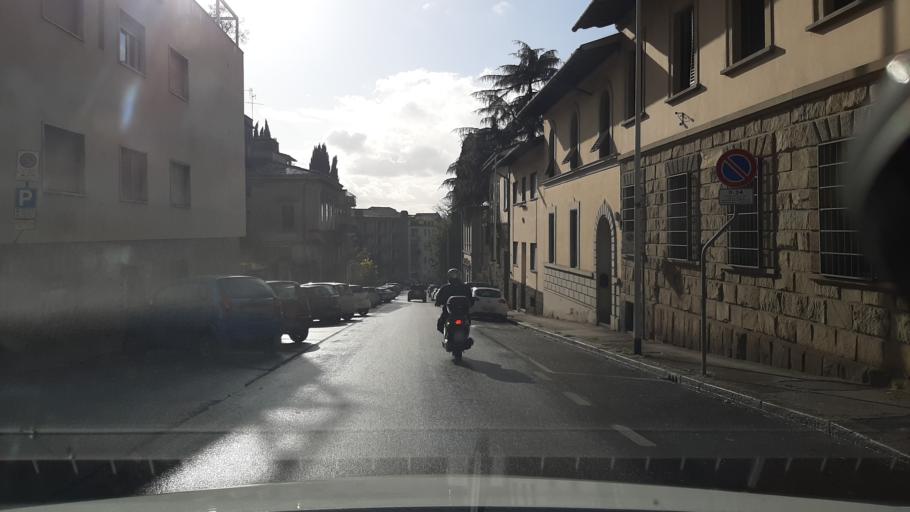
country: IT
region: Tuscany
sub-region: Province of Florence
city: Florence
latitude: 43.7908
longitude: 11.2596
